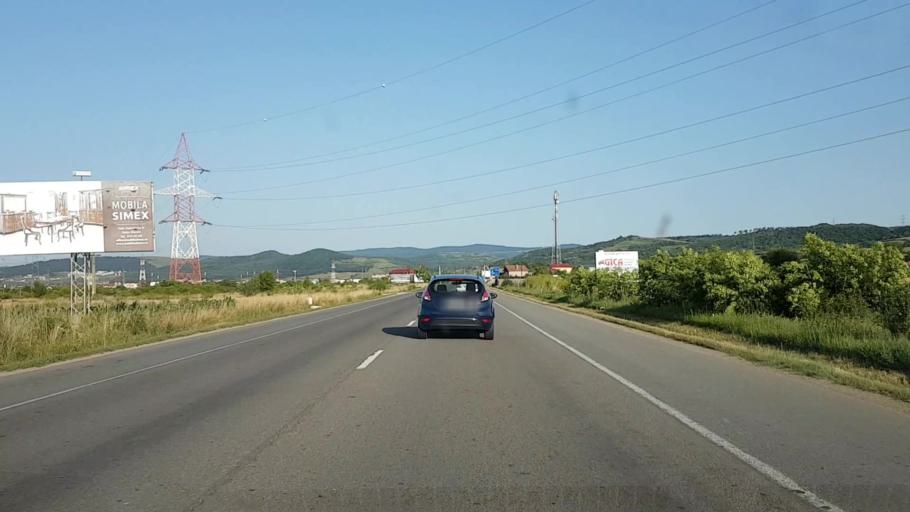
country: RO
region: Cluj
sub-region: Comuna Floresti
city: Luna de Sus
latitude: 46.7488
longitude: 23.4450
